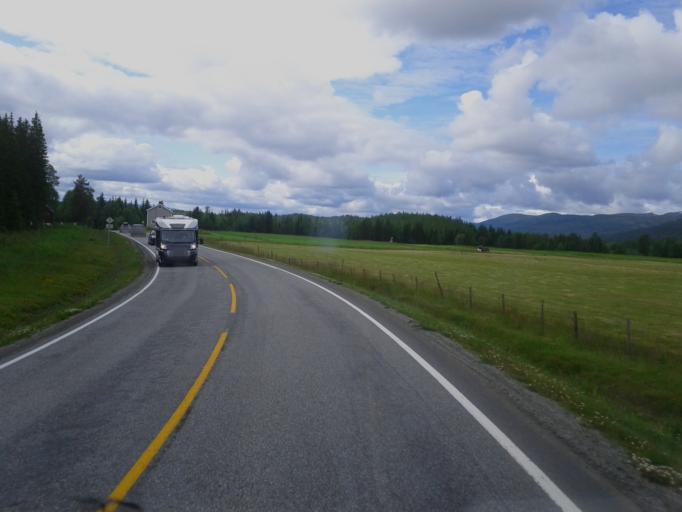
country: NO
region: Nord-Trondelag
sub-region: Hoylandet
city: Hoylandet
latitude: 64.6612
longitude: 12.6508
